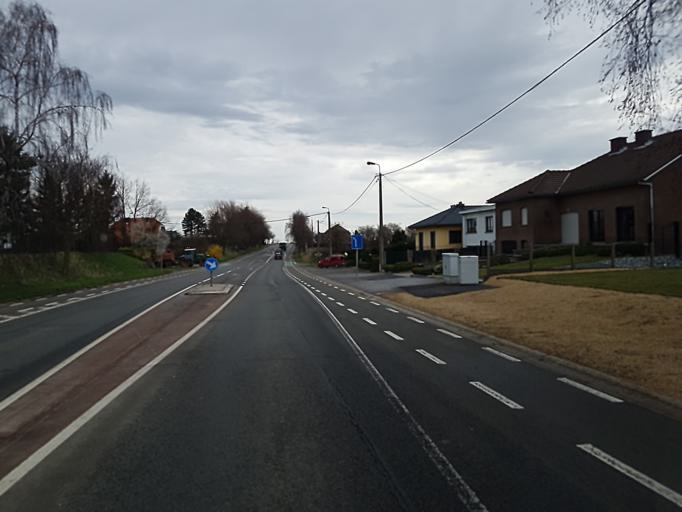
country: BE
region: Wallonia
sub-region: Province de Liege
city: Oreye
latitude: 50.7329
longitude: 5.3484
